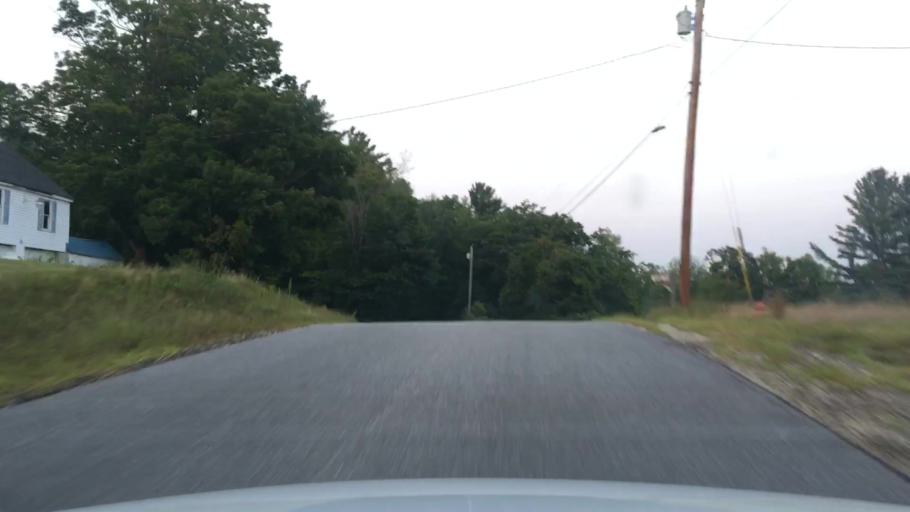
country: US
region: Maine
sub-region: Oxford County
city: Bethel
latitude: 44.4159
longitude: -70.8569
